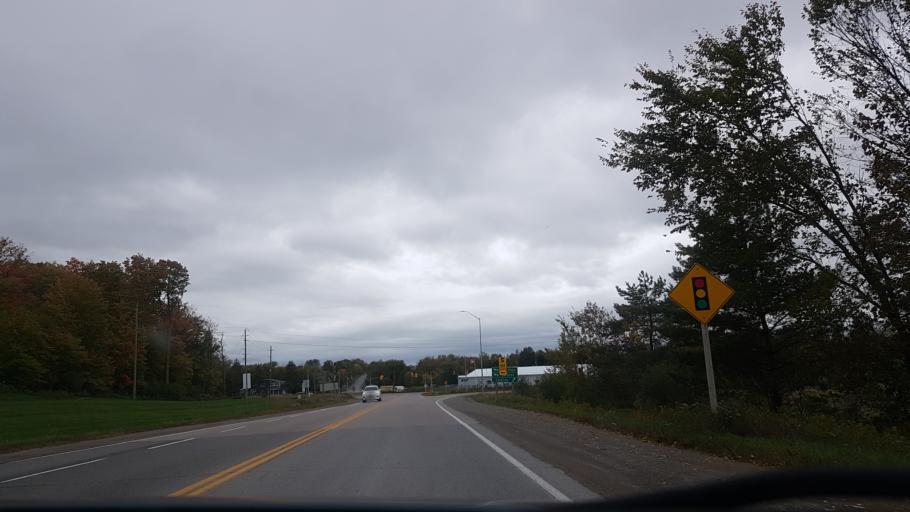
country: CA
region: Ontario
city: Peterborough
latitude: 44.2552
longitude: -78.4031
